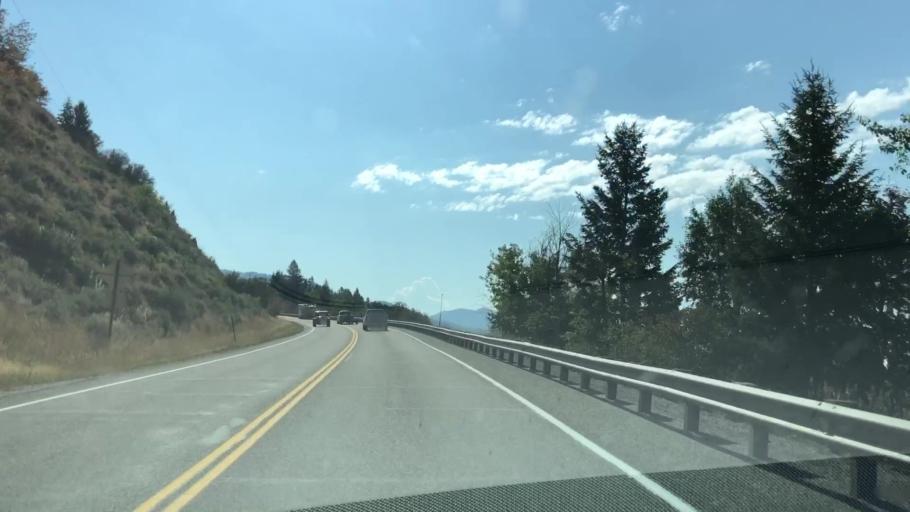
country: US
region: Idaho
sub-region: Teton County
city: Victor
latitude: 43.3125
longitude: -111.1452
